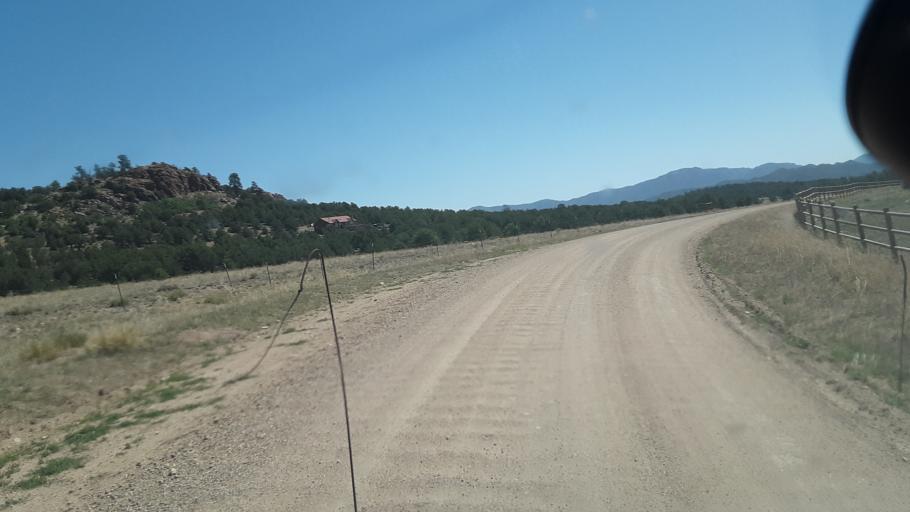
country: US
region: Colorado
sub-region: Custer County
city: Westcliffe
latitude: 38.2920
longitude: -105.4873
